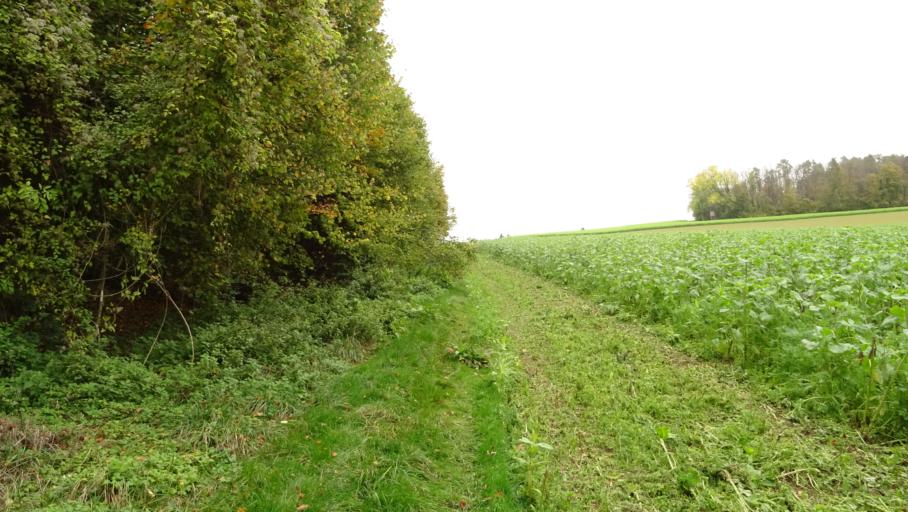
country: DE
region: Baden-Wuerttemberg
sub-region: Karlsruhe Region
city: Neckargerach
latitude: 49.3831
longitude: 9.0912
